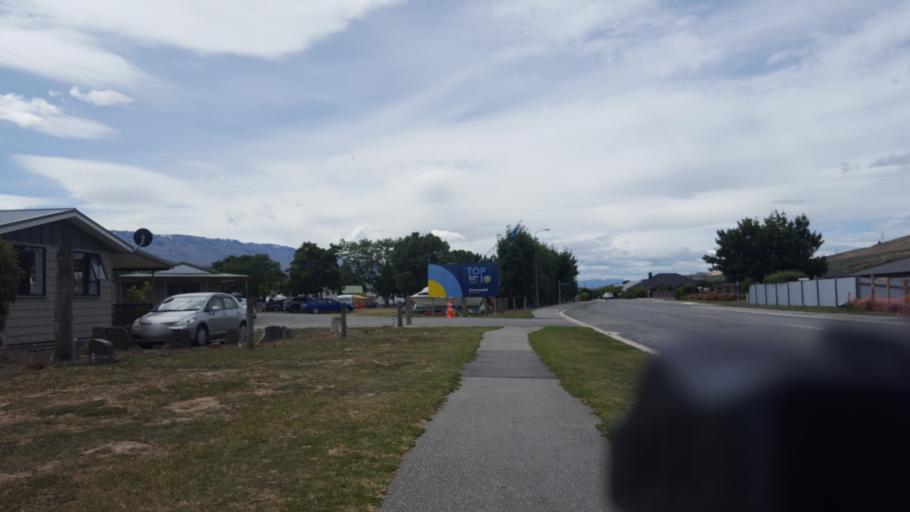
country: NZ
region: Otago
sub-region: Queenstown-Lakes District
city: Wanaka
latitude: -45.0406
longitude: 169.2146
